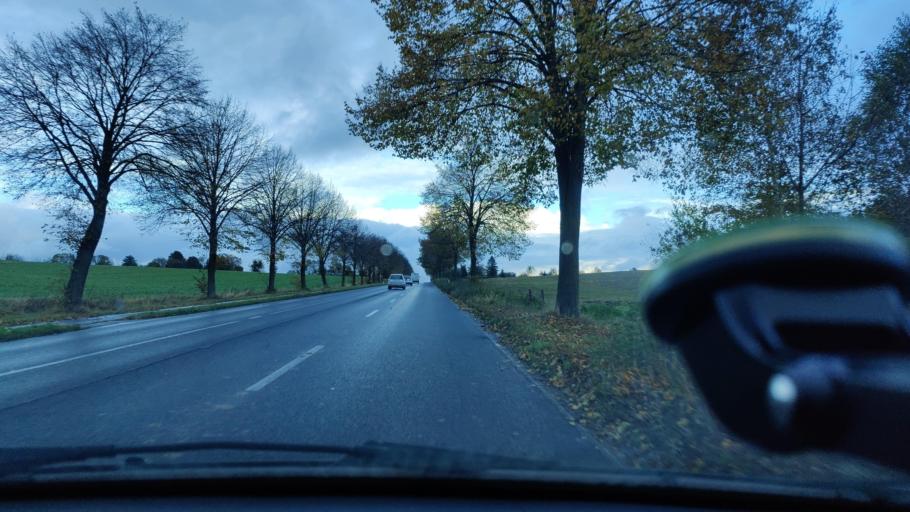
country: DE
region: North Rhine-Westphalia
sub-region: Regierungsbezirk Koln
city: Wurselen
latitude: 50.8046
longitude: 6.1371
